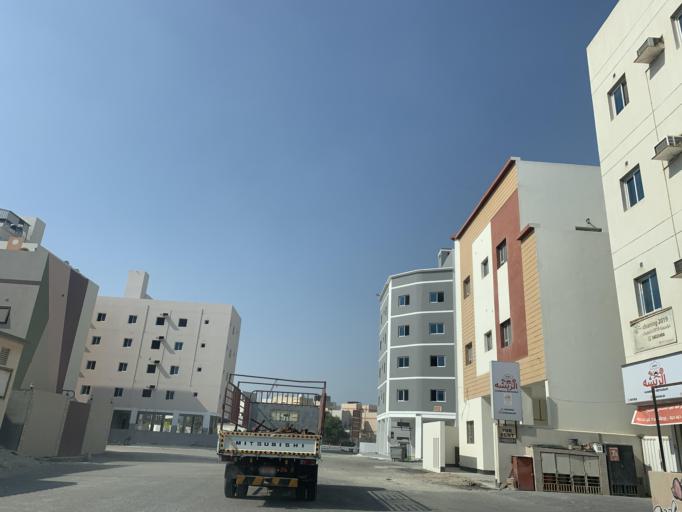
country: BH
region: Central Governorate
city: Madinat Hamad
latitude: 26.1284
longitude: 50.4890
